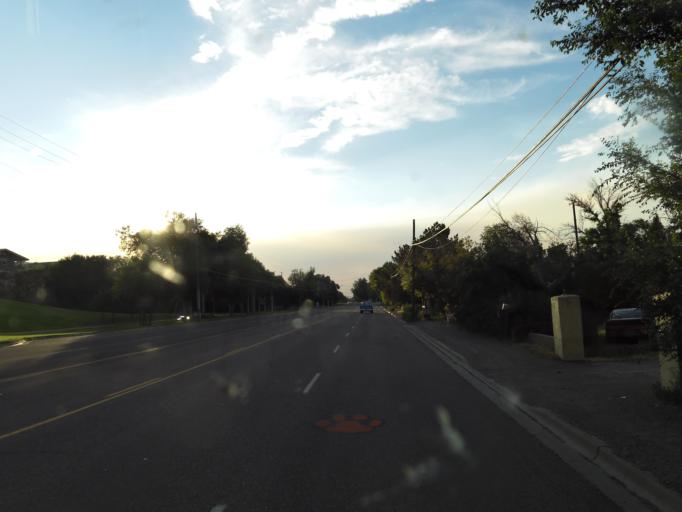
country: US
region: Idaho
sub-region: Bannock County
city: Pocatello
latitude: 42.8437
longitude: -112.4165
